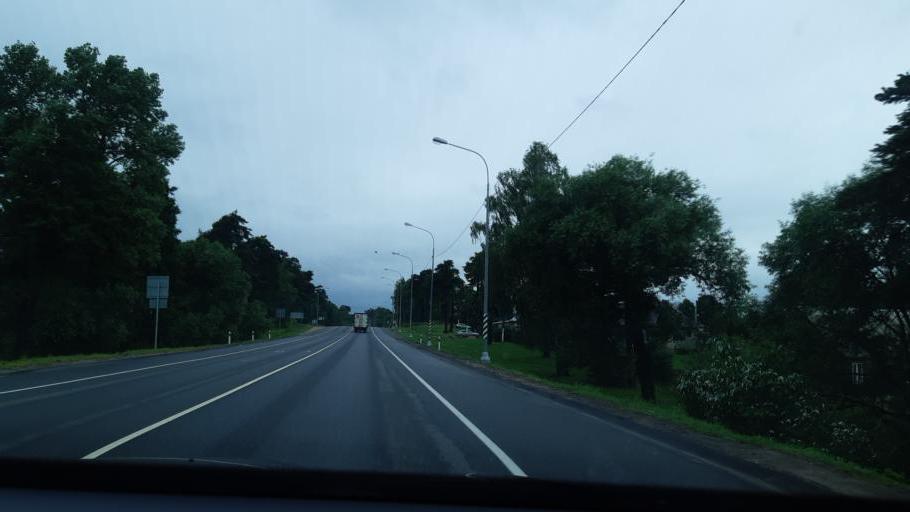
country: RU
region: Smolensk
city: Oster
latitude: 53.9927
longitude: 32.8175
